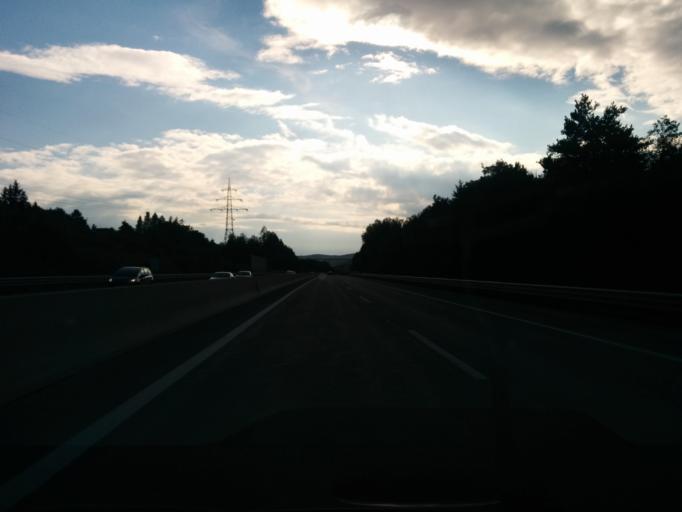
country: AT
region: Lower Austria
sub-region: Politischer Bezirk Modling
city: Laab im Walde
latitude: 48.1766
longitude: 16.1533
